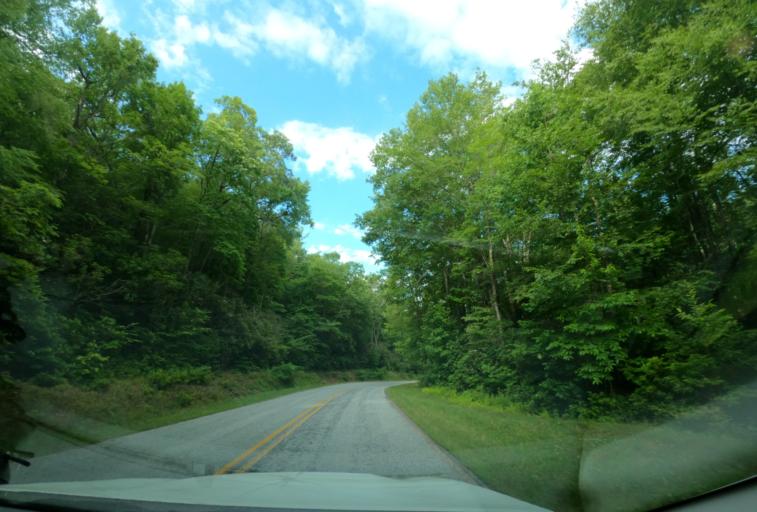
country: US
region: North Carolina
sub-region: Transylvania County
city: Brevard
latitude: 35.1715
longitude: -82.9288
